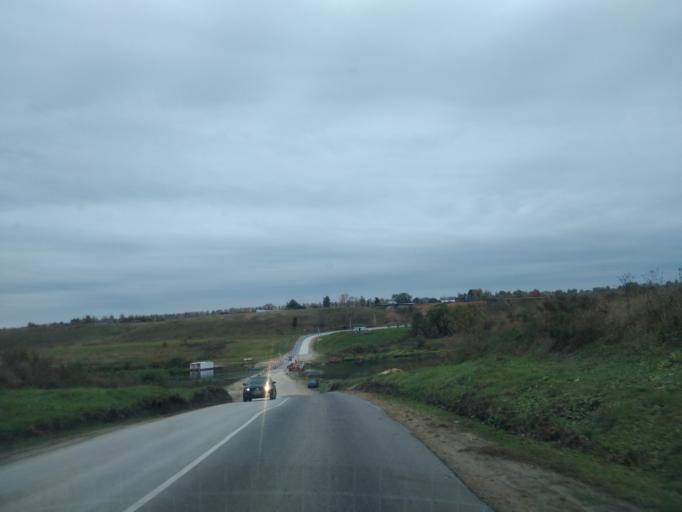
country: RU
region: Lipetsk
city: Zadonsk
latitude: 52.3221
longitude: 38.9226
